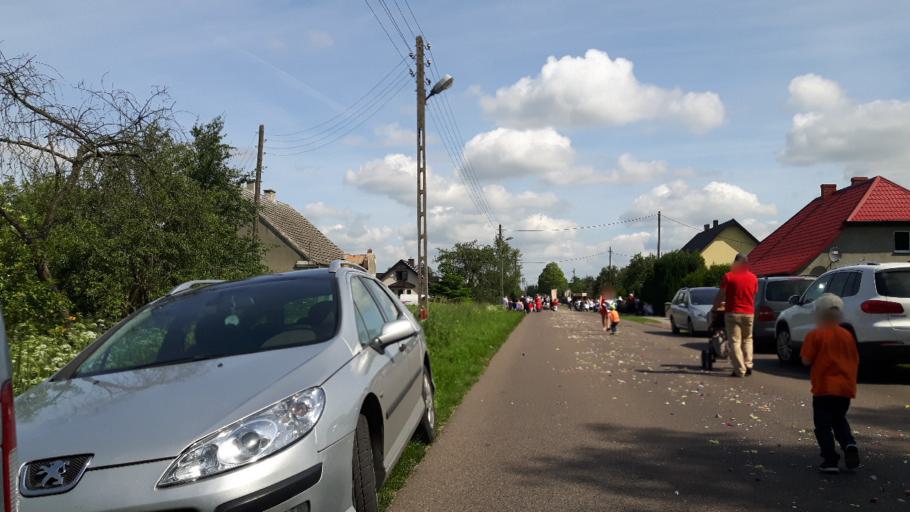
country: PL
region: West Pomeranian Voivodeship
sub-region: Powiat goleniowski
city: Goleniow
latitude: 53.4834
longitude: 14.7755
